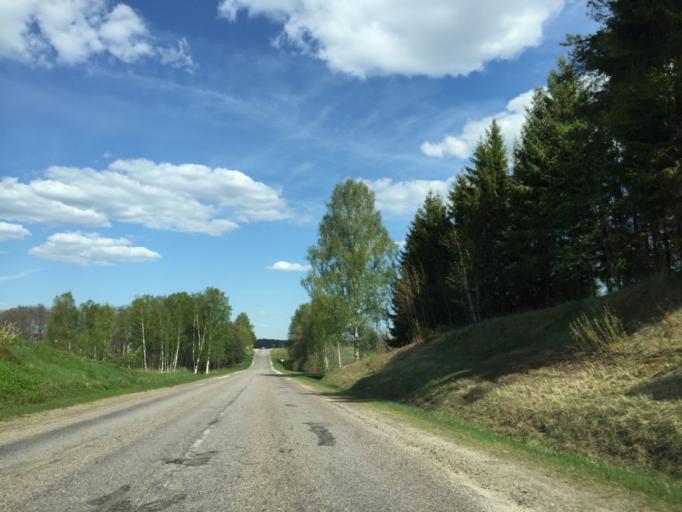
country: LV
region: Limbazu Rajons
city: Limbazi
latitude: 57.5127
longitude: 24.8051
